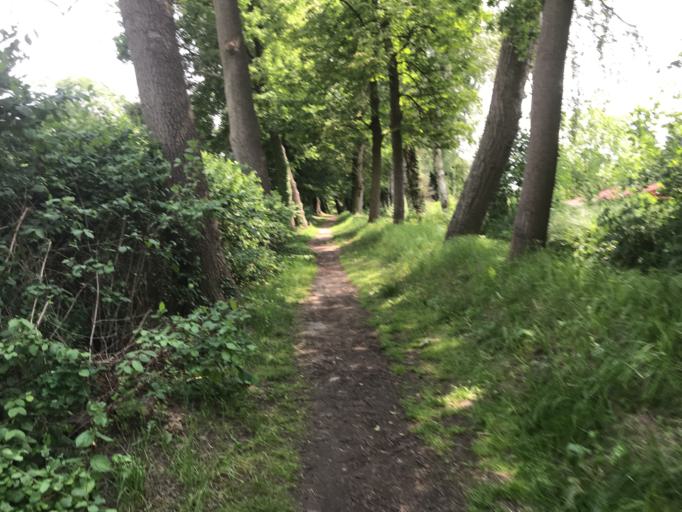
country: PL
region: West Pomeranian Voivodeship
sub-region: Powiat gryfinski
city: Chojna
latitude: 52.9613
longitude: 14.4286
